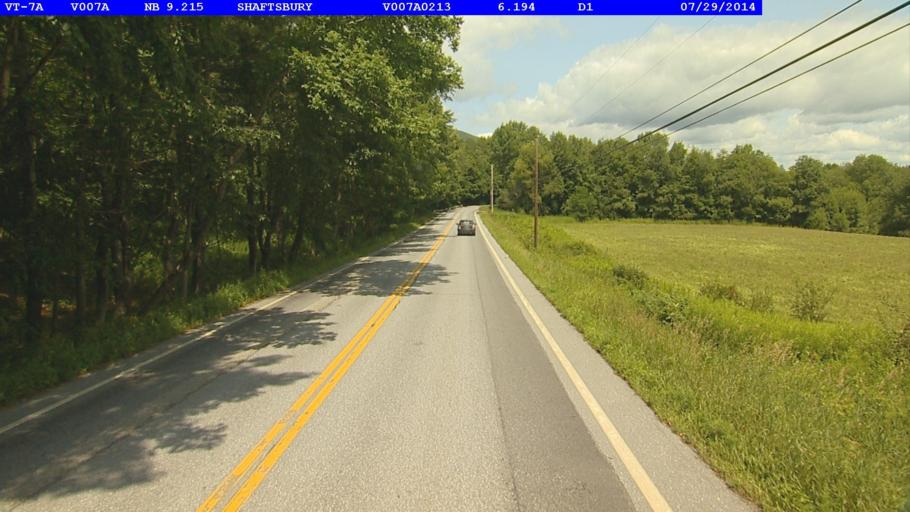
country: US
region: Vermont
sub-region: Bennington County
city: Arlington
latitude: 43.0182
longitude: -73.1907
